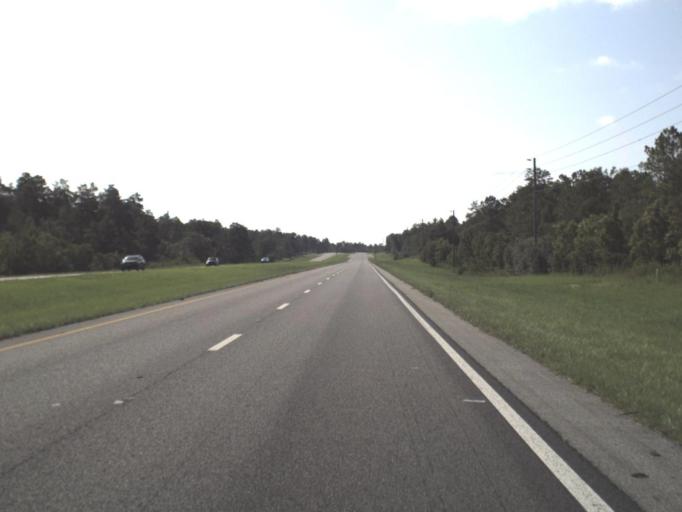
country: US
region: Florida
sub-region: Citrus County
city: Sugarmill Woods
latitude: 28.7076
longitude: -82.5262
